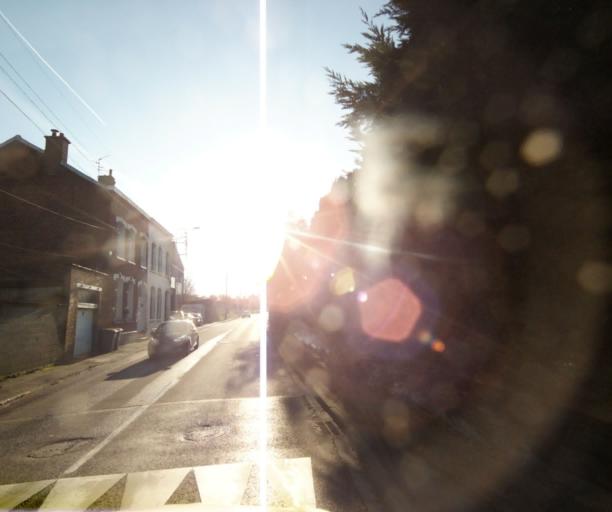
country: FR
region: Nord-Pas-de-Calais
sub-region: Departement du Nord
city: Valenciennes
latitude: 50.3470
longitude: 3.5338
